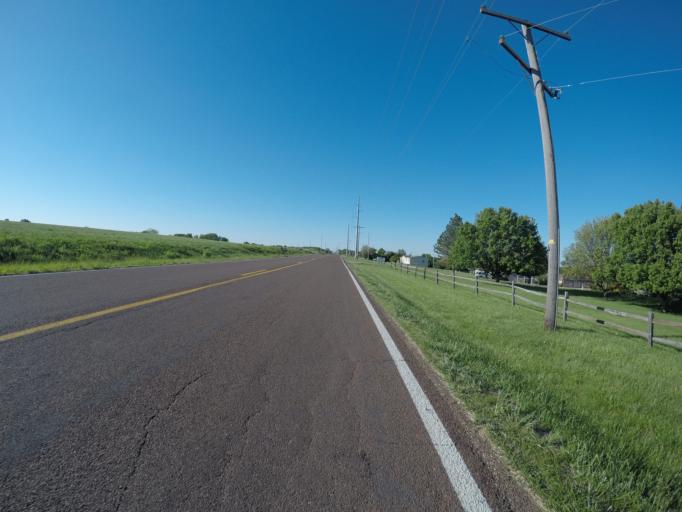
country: US
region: Kansas
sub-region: Shawnee County
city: Topeka
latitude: 39.0318
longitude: -95.5573
